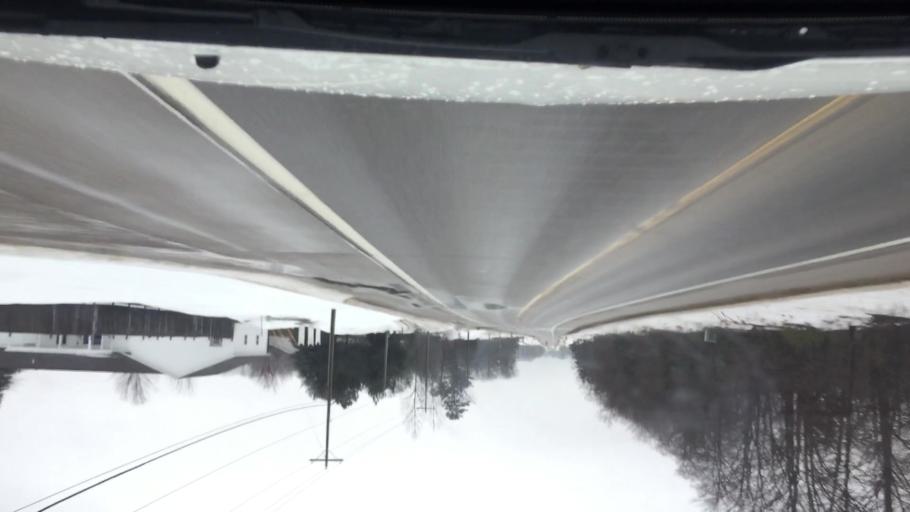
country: US
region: Michigan
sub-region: Charlevoix County
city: Charlevoix
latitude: 45.2821
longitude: -85.2374
